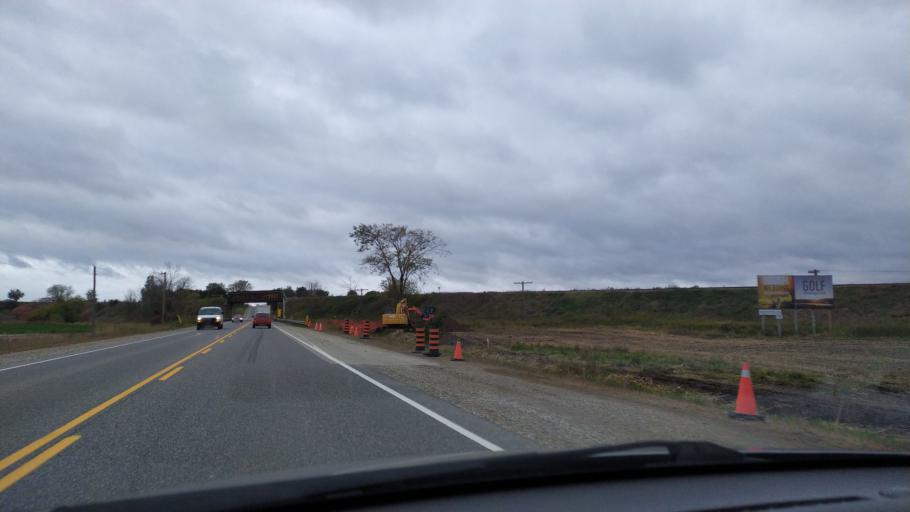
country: CA
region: Ontario
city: Stratford
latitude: 43.3691
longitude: -80.7498
